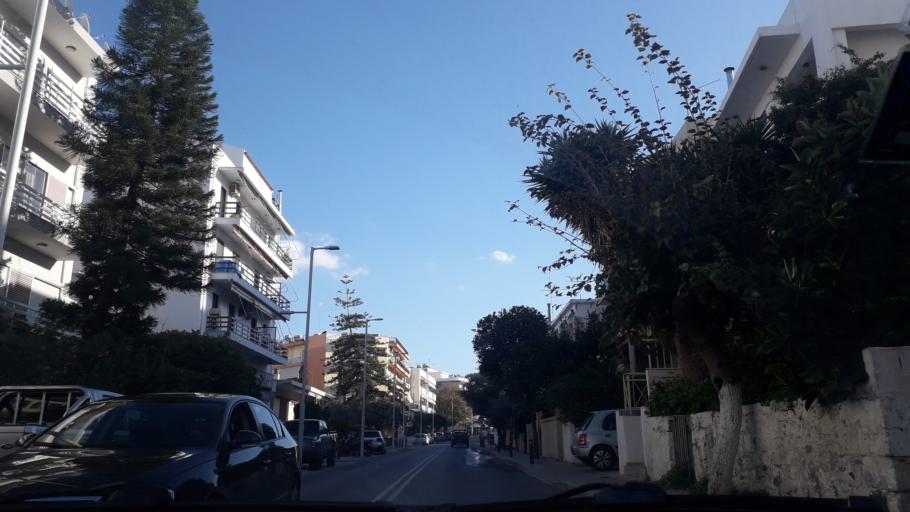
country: GR
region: Crete
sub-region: Nomos Rethymnis
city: Rethymno
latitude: 35.3646
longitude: 24.4710
